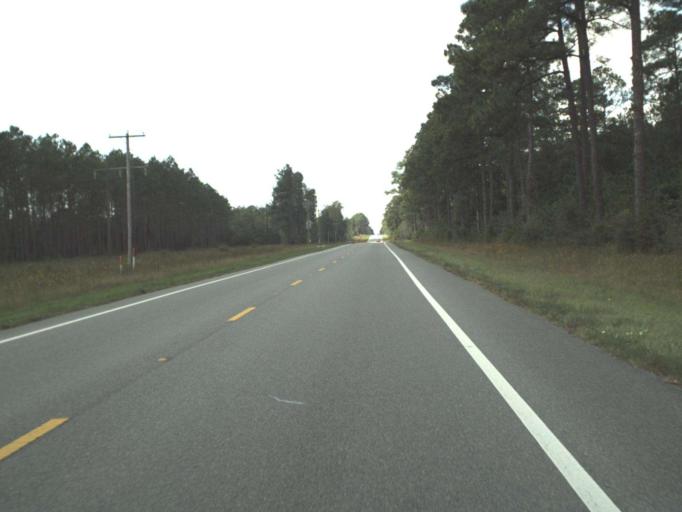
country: US
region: Florida
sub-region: Walton County
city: Freeport
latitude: 30.4755
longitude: -86.0126
